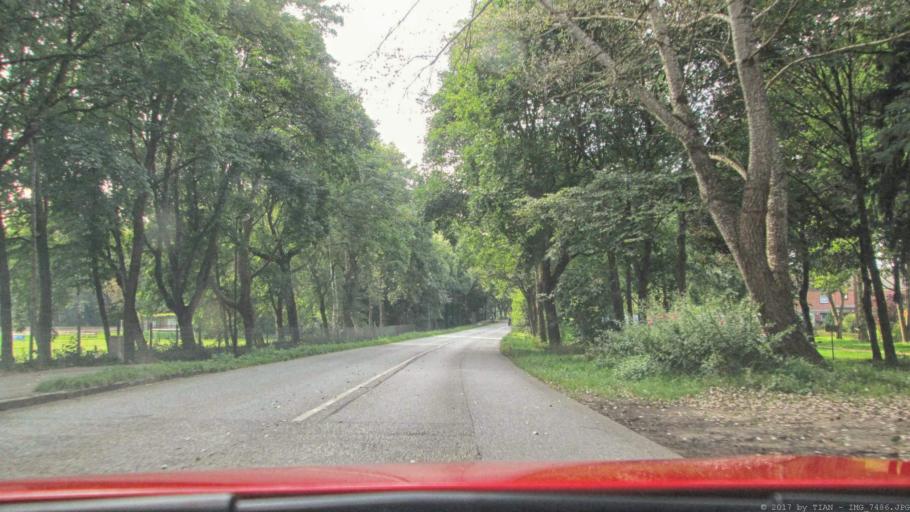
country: DE
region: Schleswig-Holstein
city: Lauenburg
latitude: 53.3736
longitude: 10.5391
